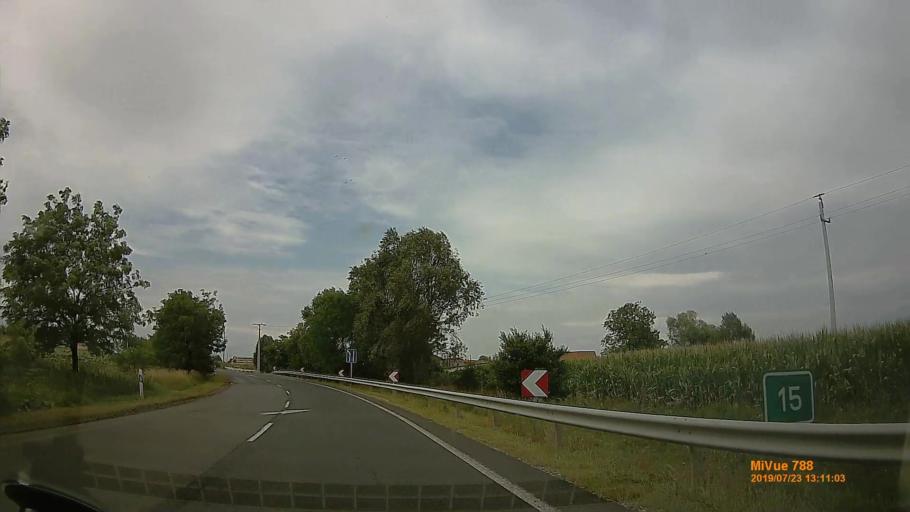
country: HU
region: Szabolcs-Szatmar-Bereg
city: Tiszavasvari
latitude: 47.9269
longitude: 21.2800
